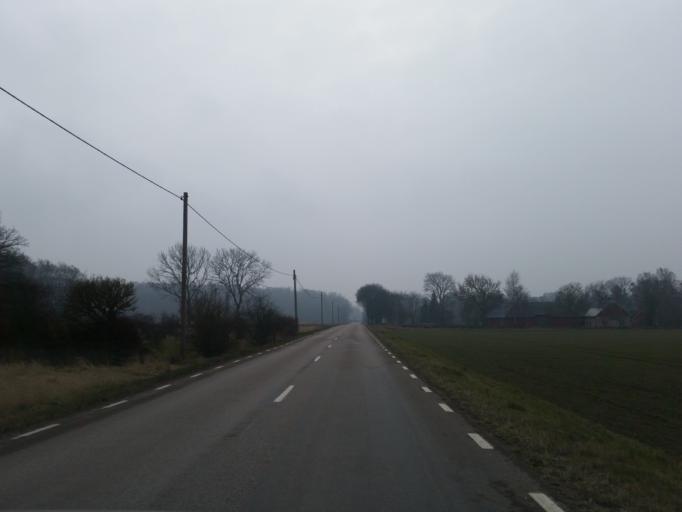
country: SE
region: Kalmar
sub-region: Morbylanga Kommun
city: Moerbylanga
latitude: 56.4342
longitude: 16.4194
